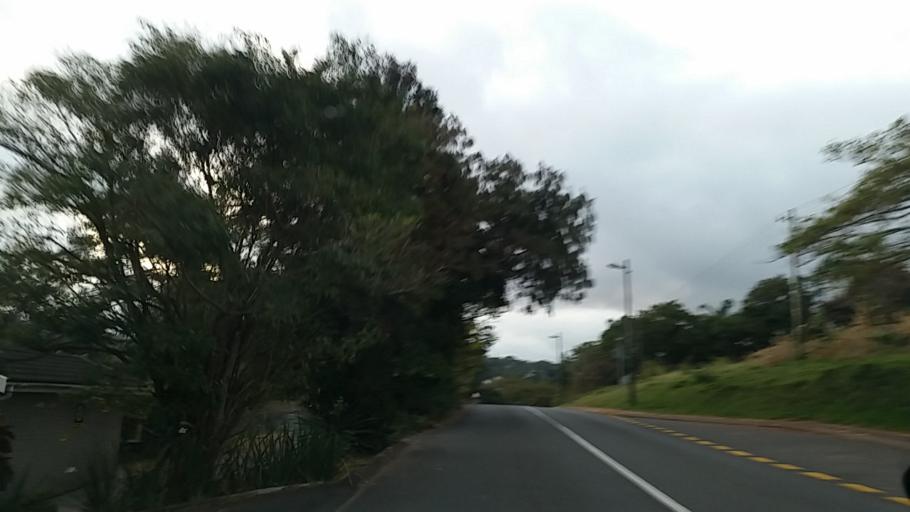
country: ZA
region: KwaZulu-Natal
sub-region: eThekwini Metropolitan Municipality
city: Berea
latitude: -29.8505
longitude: 30.9075
